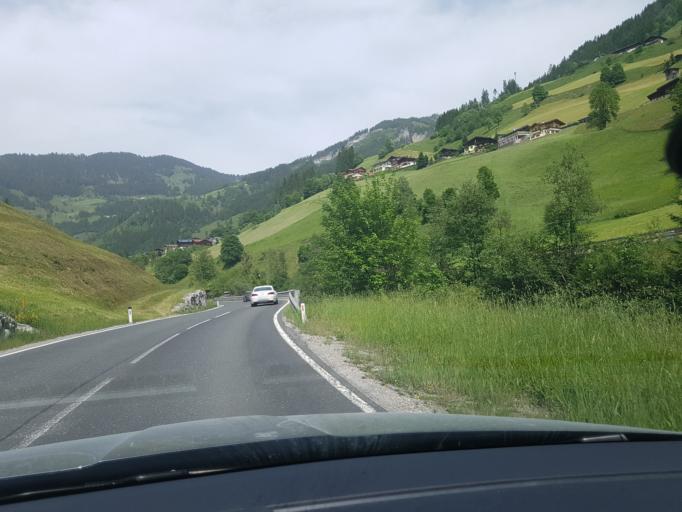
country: AT
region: Salzburg
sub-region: Politischer Bezirk Sankt Johann im Pongau
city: Schwarzach im Pongau
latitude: 47.2721
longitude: 13.2107
